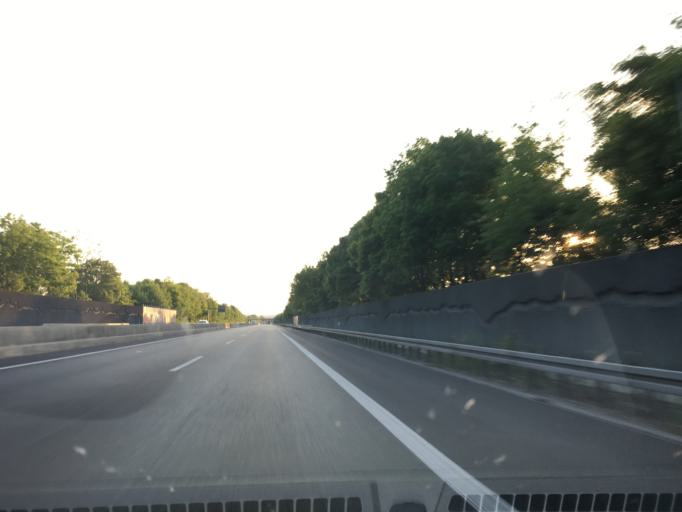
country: DE
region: North Rhine-Westphalia
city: Buende
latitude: 52.1939
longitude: 8.5289
